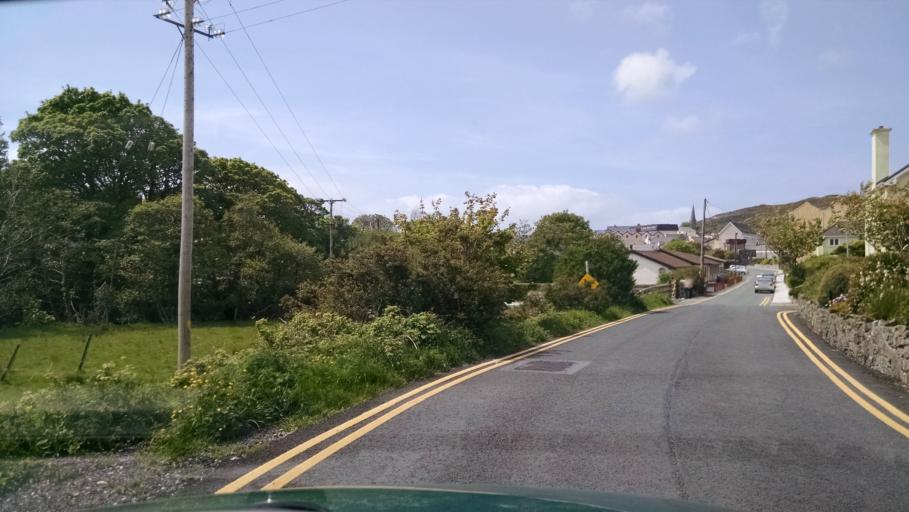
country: IE
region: Connaught
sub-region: County Galway
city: Clifden
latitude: 53.4875
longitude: -10.0140
